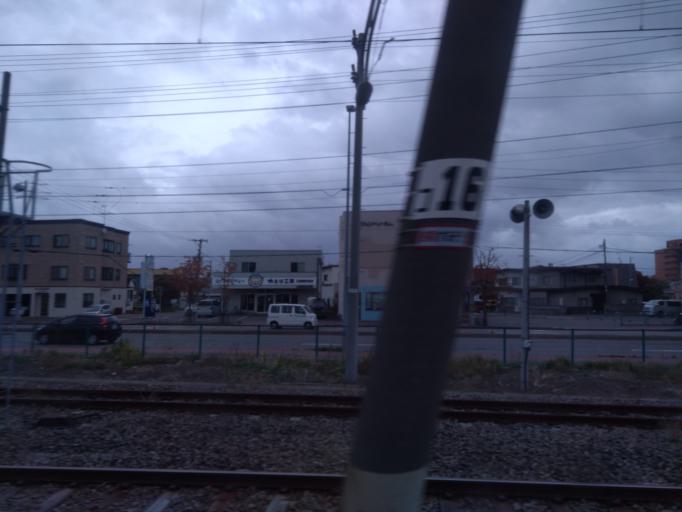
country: JP
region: Hokkaido
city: Hakodate
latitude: 41.8015
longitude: 140.7341
